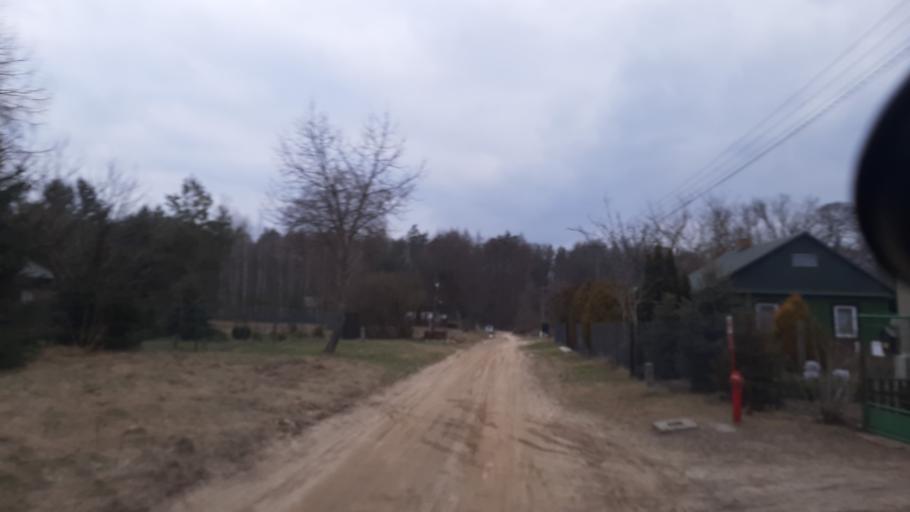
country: PL
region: Lublin Voivodeship
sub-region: Powiat lubelski
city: Garbow
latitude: 51.4000
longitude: 22.3902
